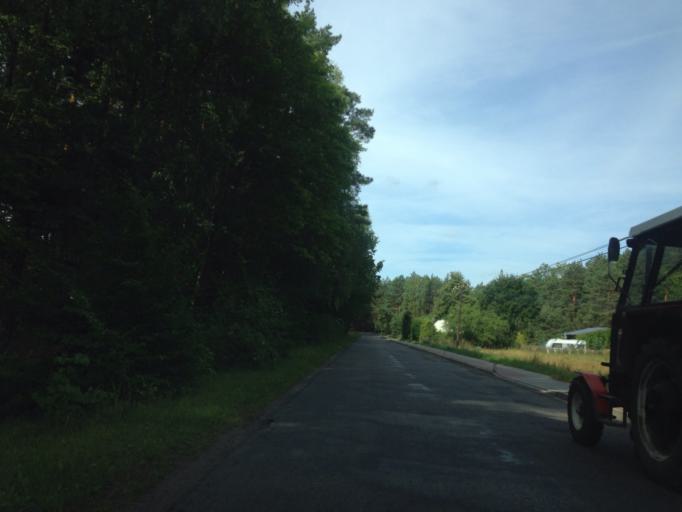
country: PL
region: Kujawsko-Pomorskie
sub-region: Powiat tucholski
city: Sliwice
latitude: 53.7218
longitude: 18.1995
